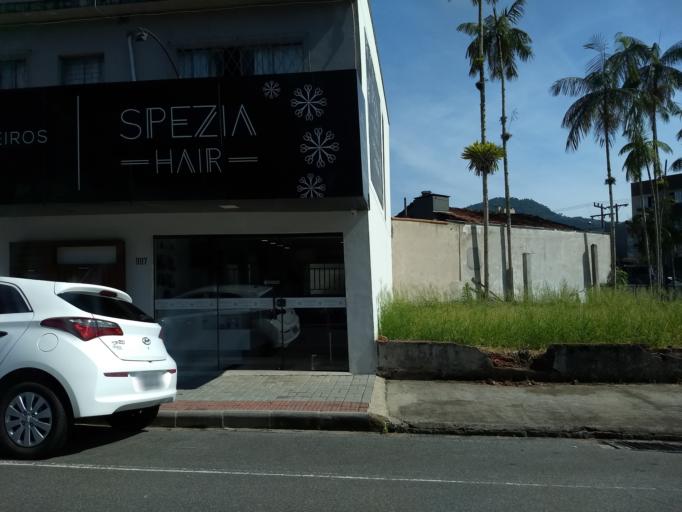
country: BR
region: Santa Catarina
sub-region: Jaragua Do Sul
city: Jaragua do Sul
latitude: -26.4919
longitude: -49.0732
